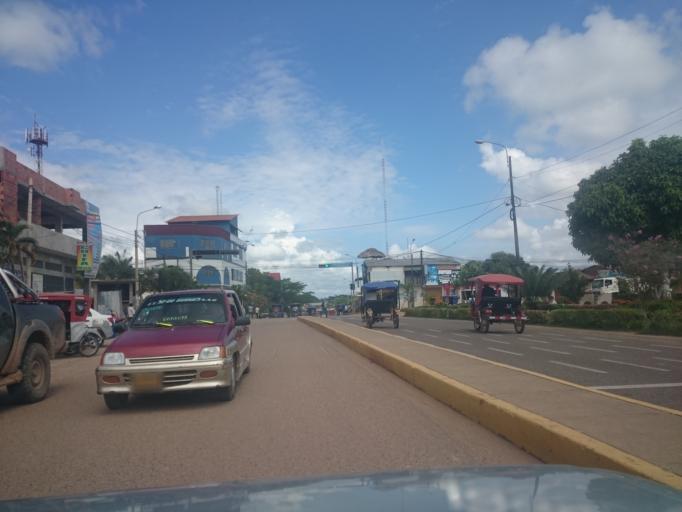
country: PE
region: Ucayali
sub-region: Provincia de Coronel Portillo
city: Puerto Callao
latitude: -8.3551
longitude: -74.5763
